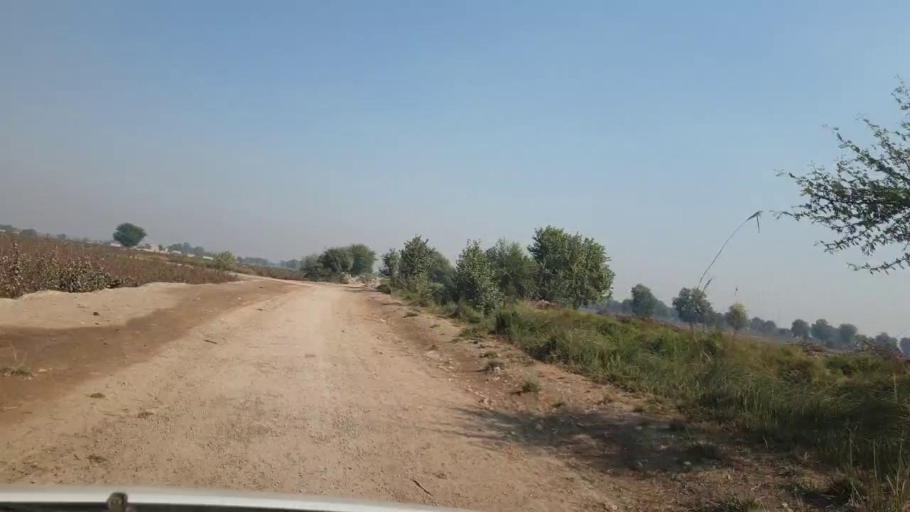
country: PK
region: Sindh
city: Bhan
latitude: 26.6192
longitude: 67.7622
